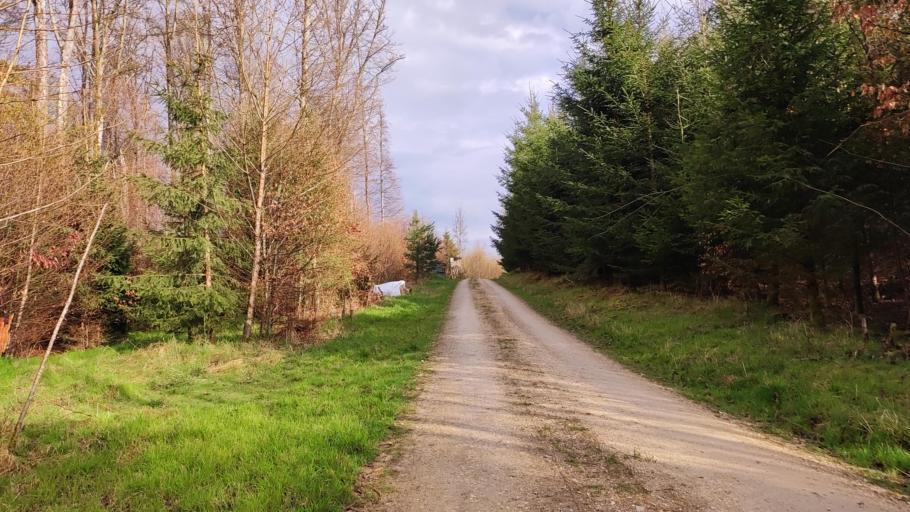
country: DE
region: Bavaria
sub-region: Swabia
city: Zusmarshausen
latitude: 48.4193
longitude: 10.6192
